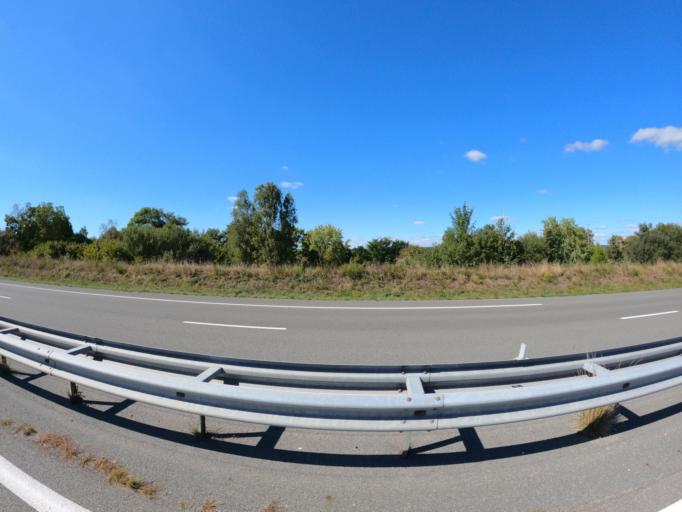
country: FR
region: Limousin
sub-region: Departement de la Creuse
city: Chambon-sur-Voueize
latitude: 46.2817
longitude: 2.3980
